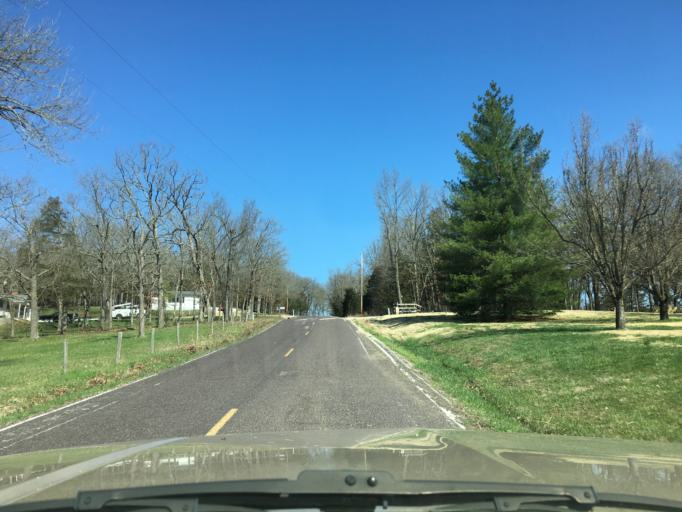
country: US
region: Missouri
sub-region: Franklin County
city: Gerald
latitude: 38.5304
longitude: -91.3321
